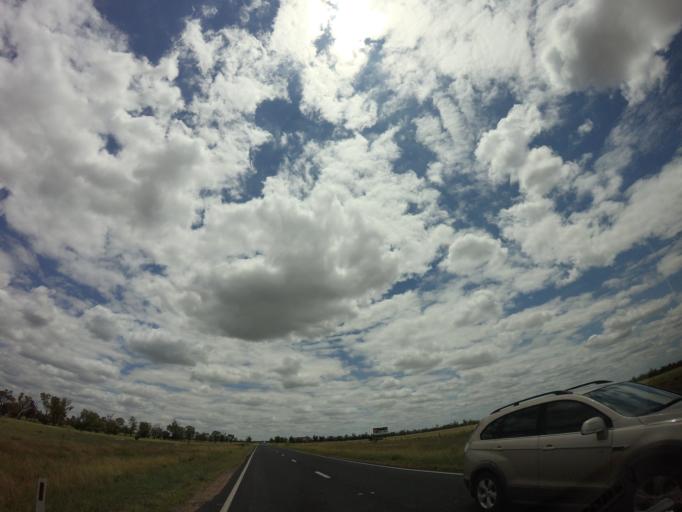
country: AU
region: New South Wales
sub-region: Moree Plains
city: Boggabilla
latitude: -28.6343
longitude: 150.3444
